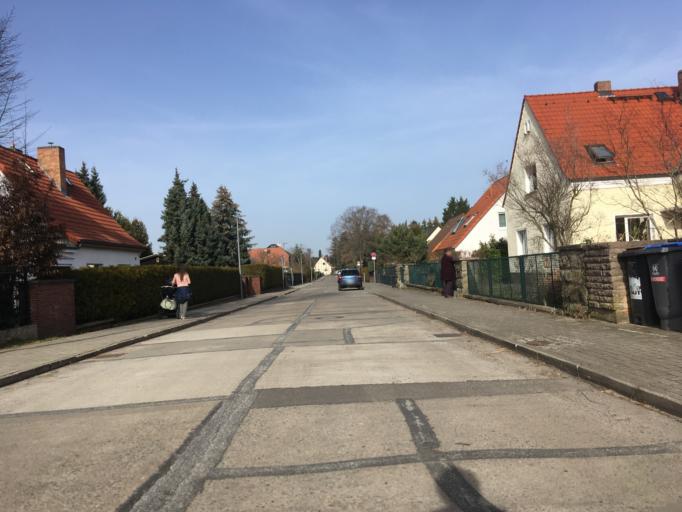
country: DE
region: Berlin
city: Bohnsdorf
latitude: 52.3961
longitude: 13.5684
